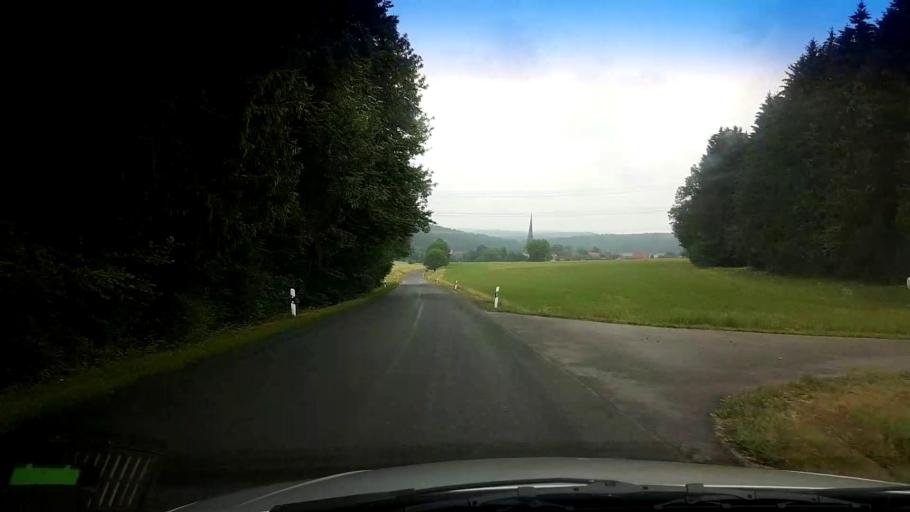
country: DE
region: Bavaria
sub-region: Upper Franconia
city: Wattendorf
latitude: 50.0510
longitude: 11.1297
